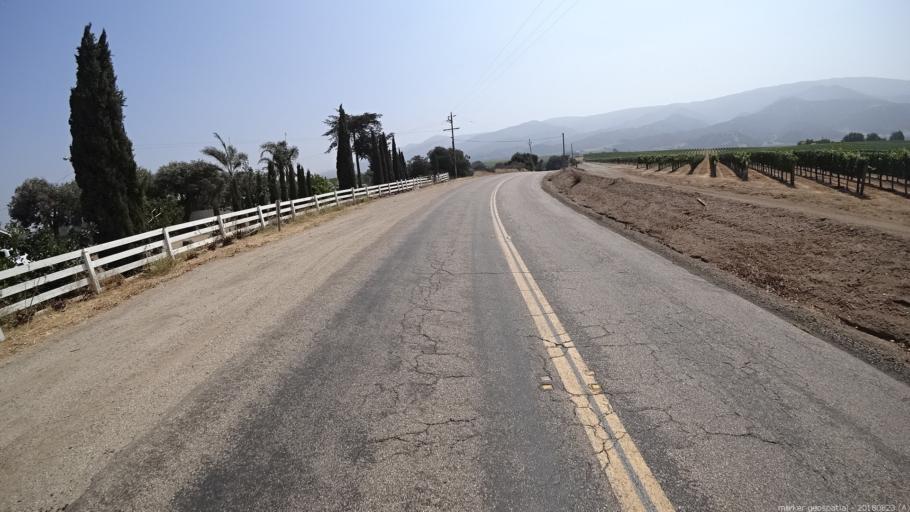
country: US
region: California
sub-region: Monterey County
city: Gonzales
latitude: 36.4441
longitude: -121.4313
